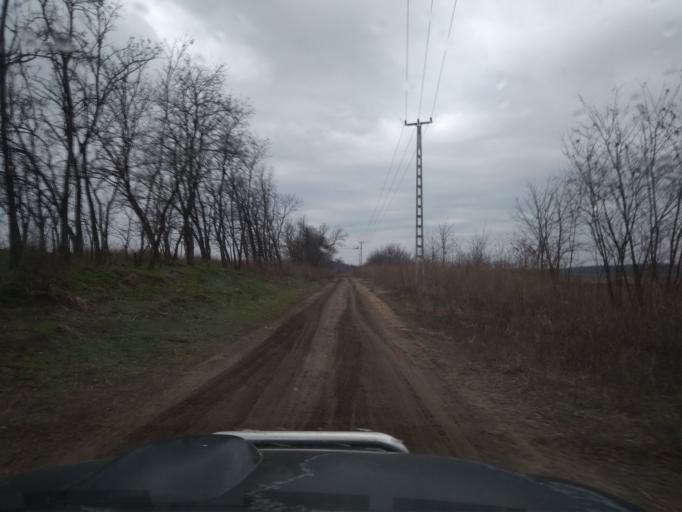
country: HU
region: Szabolcs-Szatmar-Bereg
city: Nyirpazony
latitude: 48.0007
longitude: 21.7891
